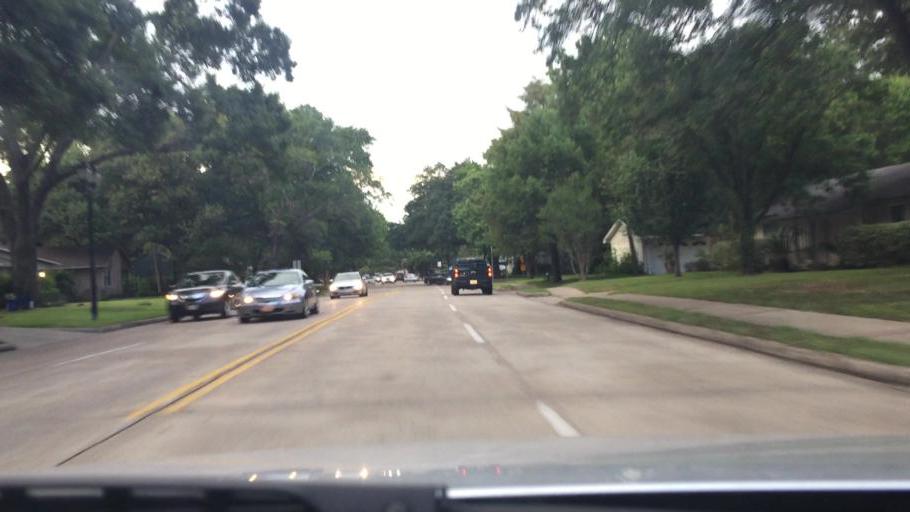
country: US
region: Texas
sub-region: Harris County
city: Hunters Creek Village
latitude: 29.7415
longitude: -95.4770
